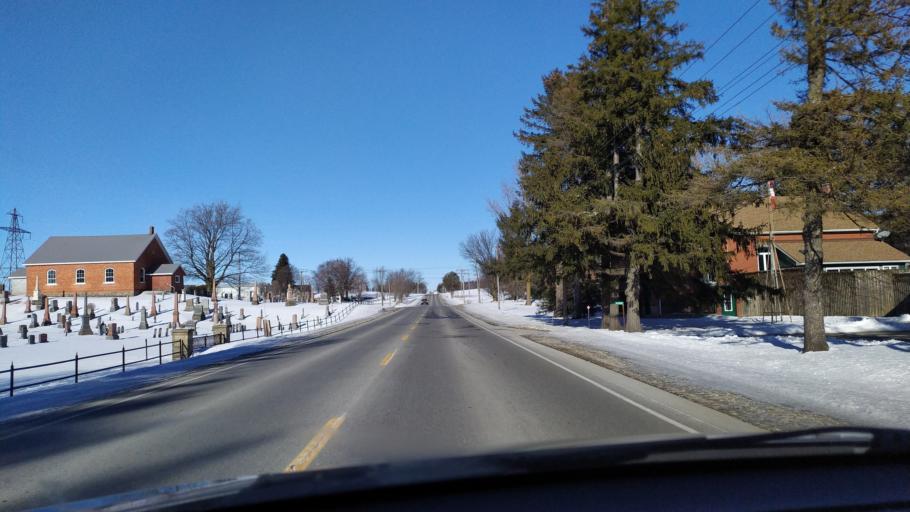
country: CA
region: Ontario
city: Stratford
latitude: 43.3868
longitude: -80.8372
